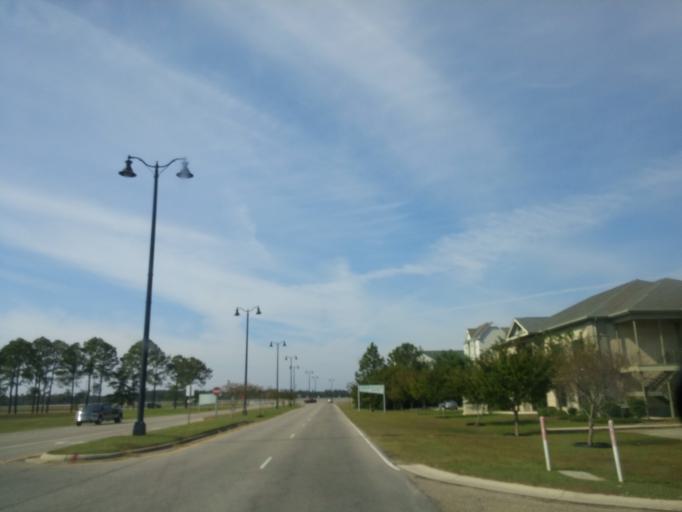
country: US
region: Mississippi
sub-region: Harrison County
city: West Gulfport
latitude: 30.4153
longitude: -89.0734
